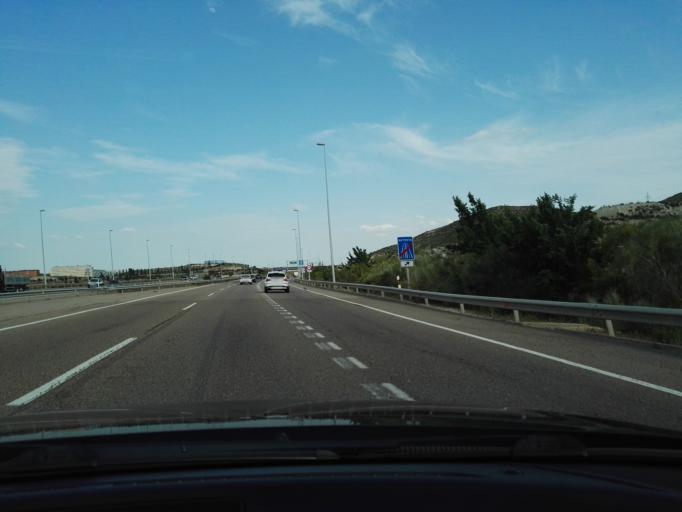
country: ES
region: Aragon
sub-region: Provincia de Zaragoza
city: Montecanal
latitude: 41.6177
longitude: -0.9398
